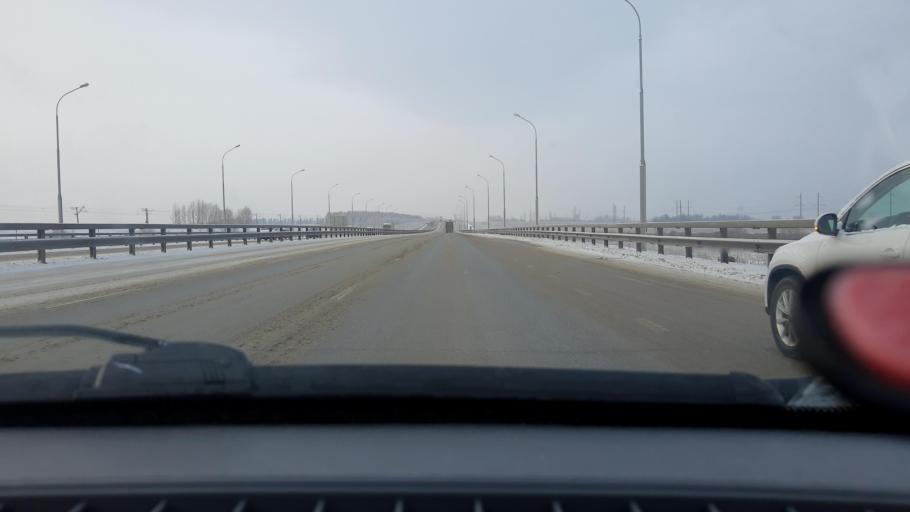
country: RU
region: Bashkortostan
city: Kabakovo
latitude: 54.6642
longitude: 56.1514
